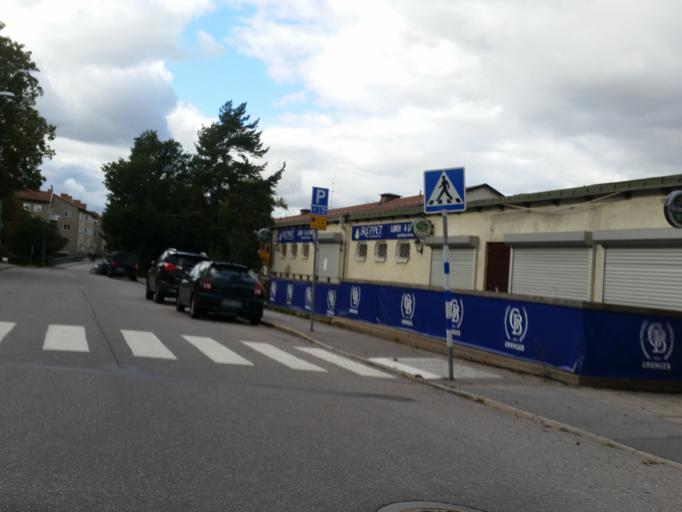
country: SE
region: Stockholm
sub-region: Stockholms Kommun
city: OEstermalm
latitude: 59.2874
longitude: 18.1083
